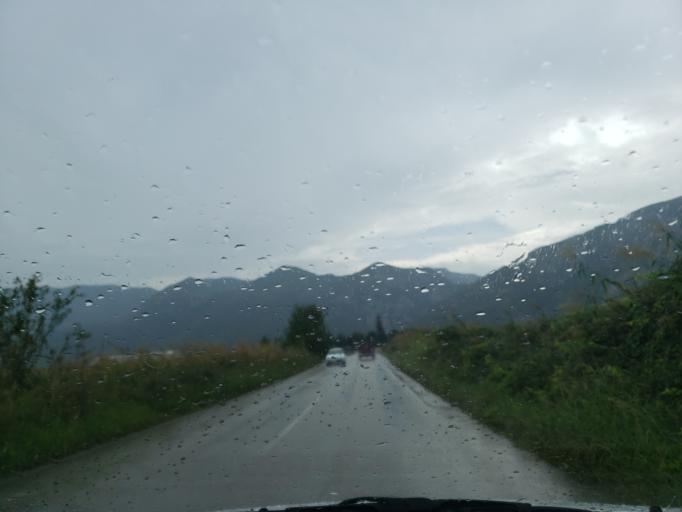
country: GR
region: Central Greece
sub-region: Nomos Fthiotidos
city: Anthili
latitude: 38.8075
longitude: 22.4425
